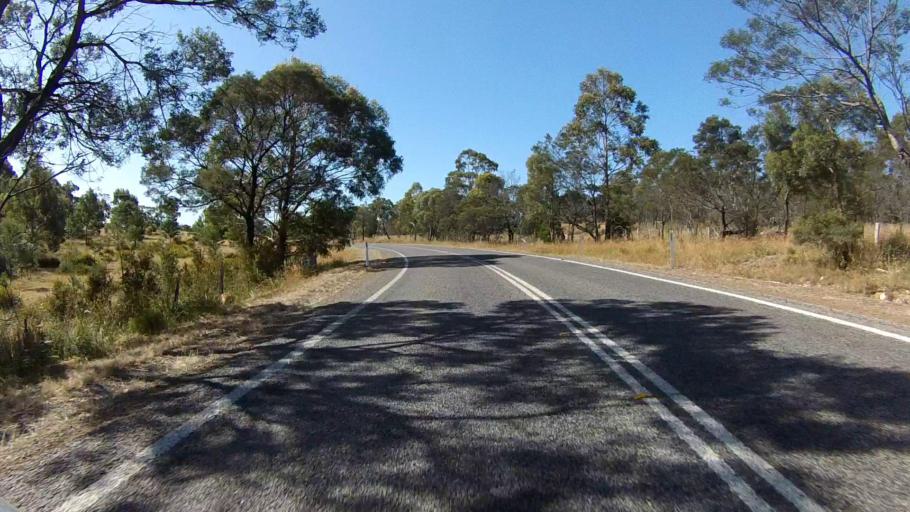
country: AU
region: Tasmania
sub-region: Sorell
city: Sorell
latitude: -42.3288
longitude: 147.9458
